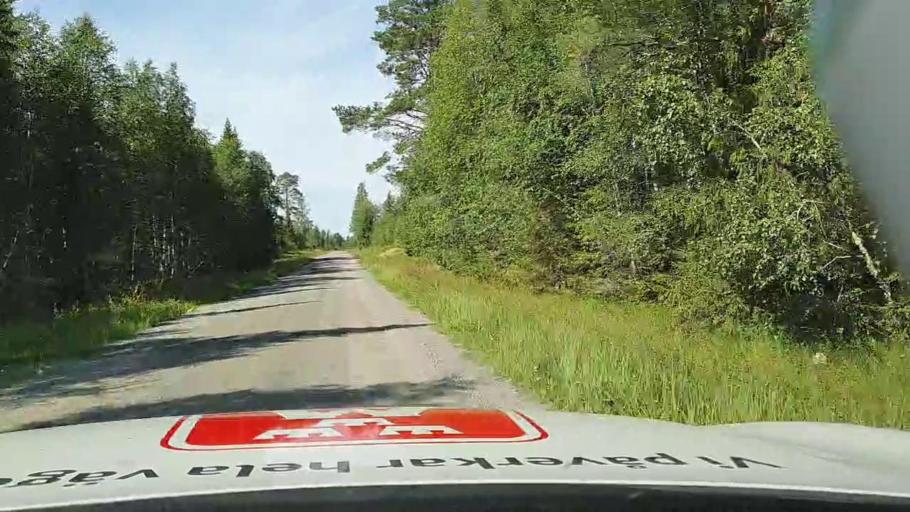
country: SE
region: Jaemtland
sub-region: Stroemsunds Kommun
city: Stroemsund
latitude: 63.7107
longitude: 15.3090
